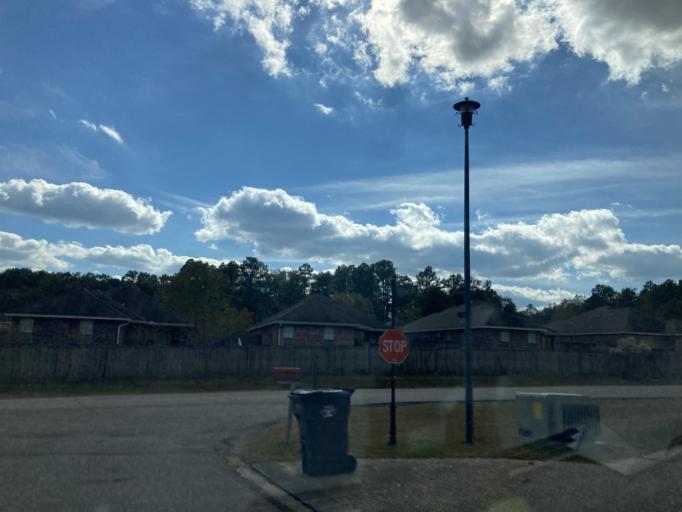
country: US
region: Mississippi
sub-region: Lamar County
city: Arnold Line
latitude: 31.3420
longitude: -89.3956
